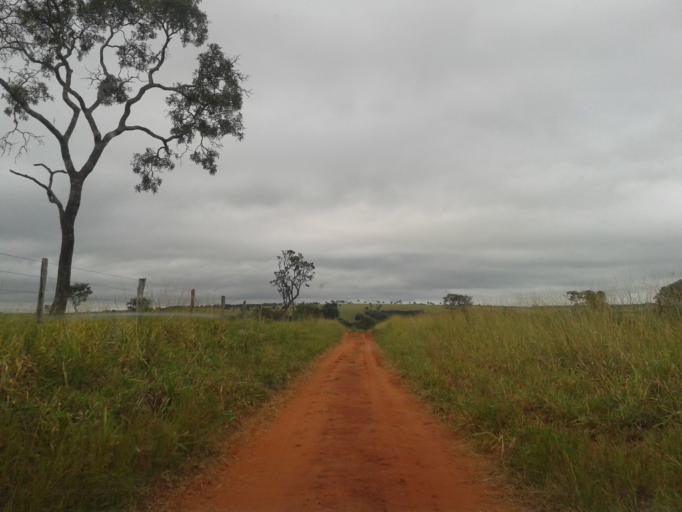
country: BR
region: Minas Gerais
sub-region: Campina Verde
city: Campina Verde
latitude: -19.4200
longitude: -49.6464
